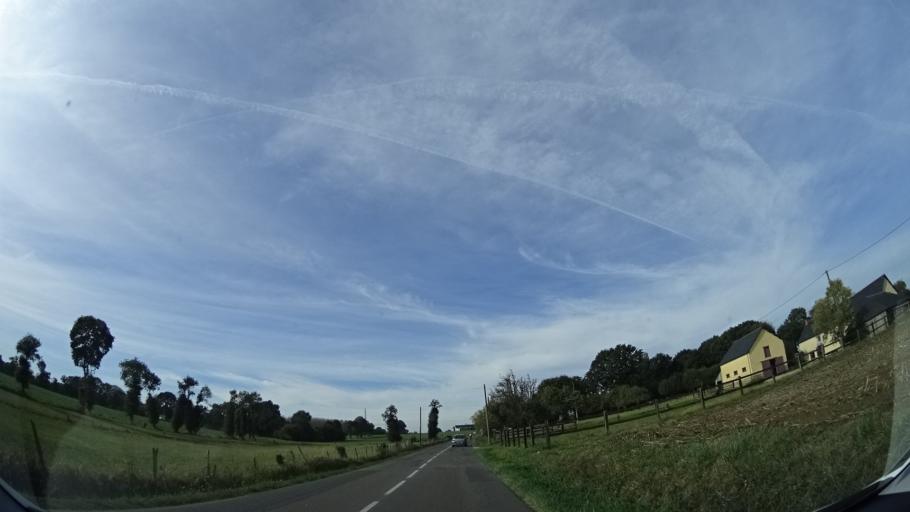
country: FR
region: Brittany
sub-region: Departement d'Ille-et-Vilaine
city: Melesse
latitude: 48.2167
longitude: -1.7238
